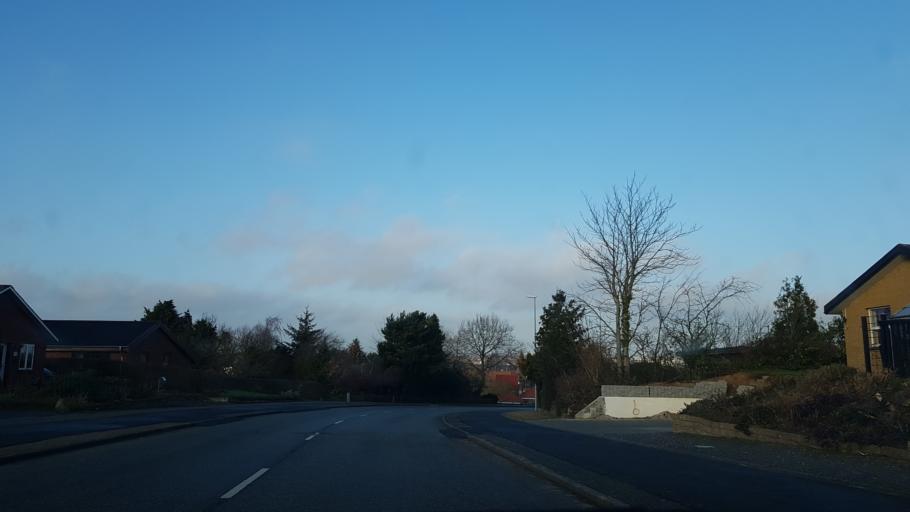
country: DK
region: South Denmark
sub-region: Haderslev Kommune
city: Haderslev
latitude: 55.2387
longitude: 9.4990
